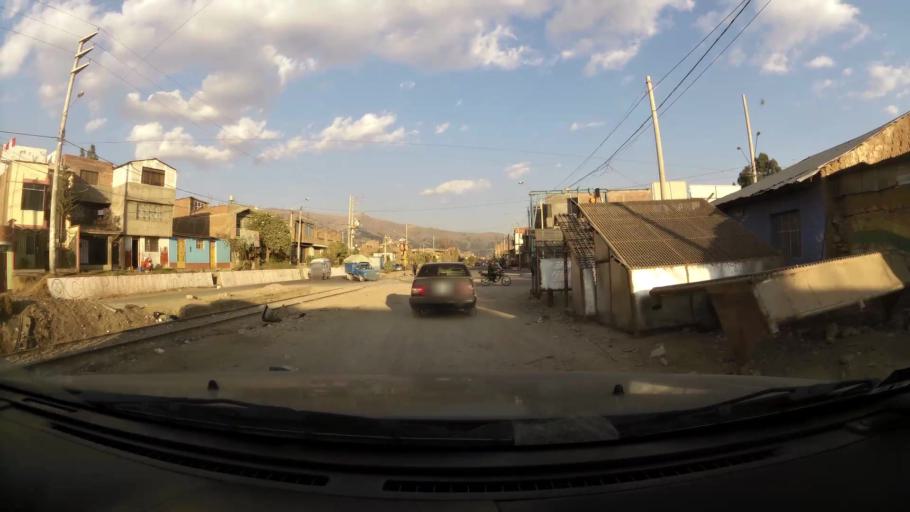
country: PE
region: Junin
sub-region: Provincia de Huancayo
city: El Tambo
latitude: -12.0412
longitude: -75.2227
